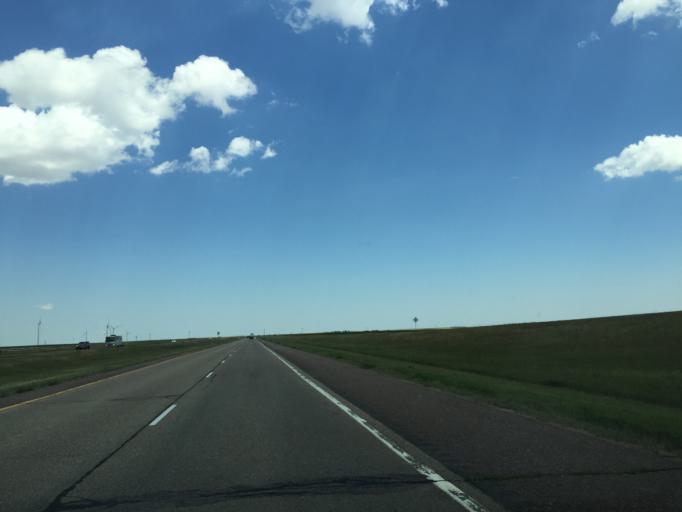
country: US
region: Colorado
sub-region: Lincoln County
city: Hugo
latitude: 39.2780
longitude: -103.4340
